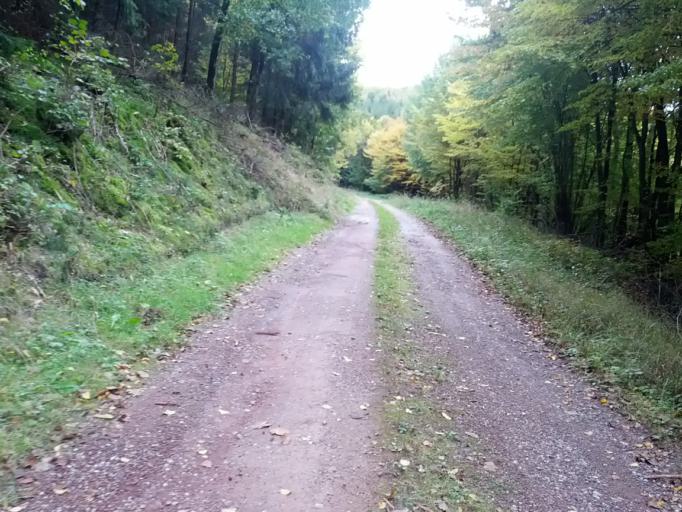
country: DE
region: Thuringia
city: Eisenach
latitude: 50.9742
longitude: 10.2756
